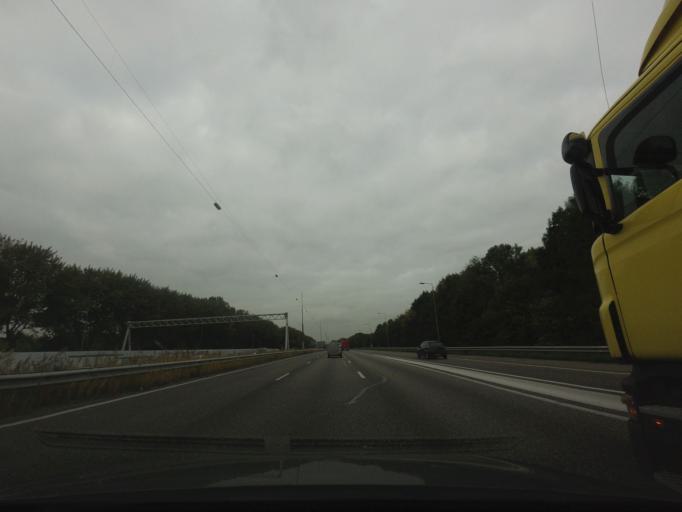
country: NL
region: North Holland
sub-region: Gemeente Waterland
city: Broek in Waterland
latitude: 52.3924
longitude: 4.9649
